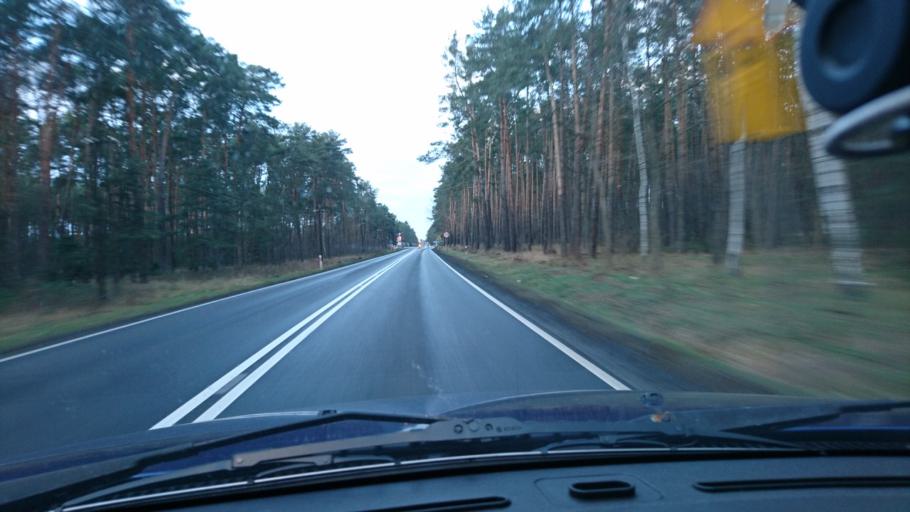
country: PL
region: Greater Poland Voivodeship
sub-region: Powiat kepinski
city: Kepno
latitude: 51.3381
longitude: 17.9534
